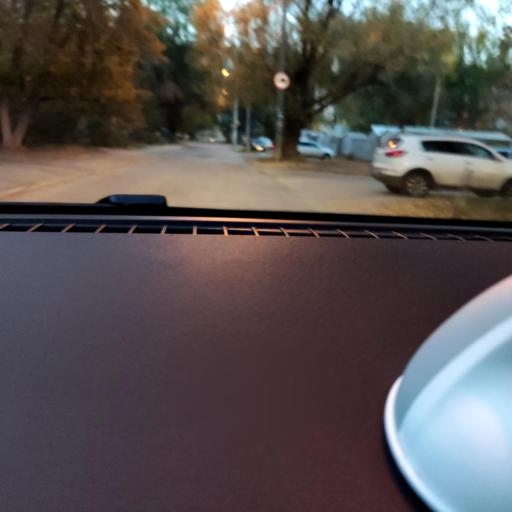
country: RU
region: Samara
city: Samara
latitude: 53.2073
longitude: 50.1836
